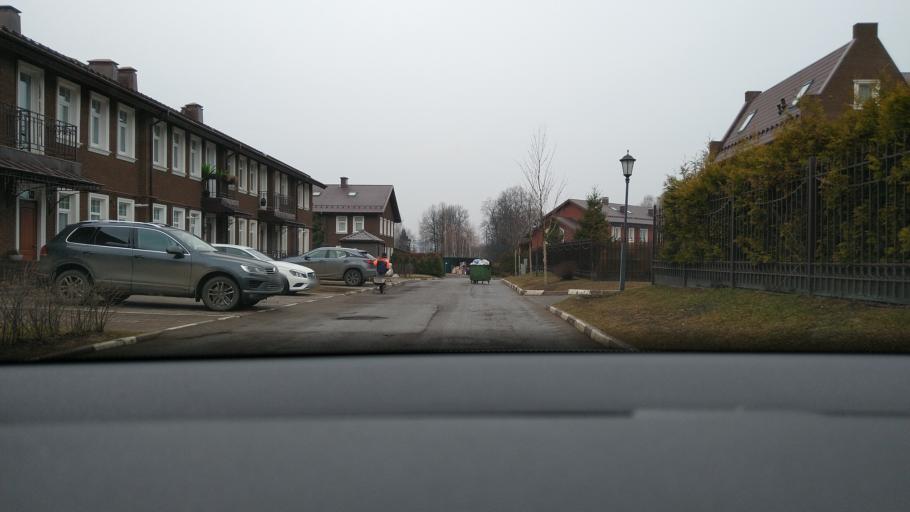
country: RU
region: Moskovskaya
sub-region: Leninskiy Rayon
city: Vnukovo
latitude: 55.6170
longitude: 37.3233
